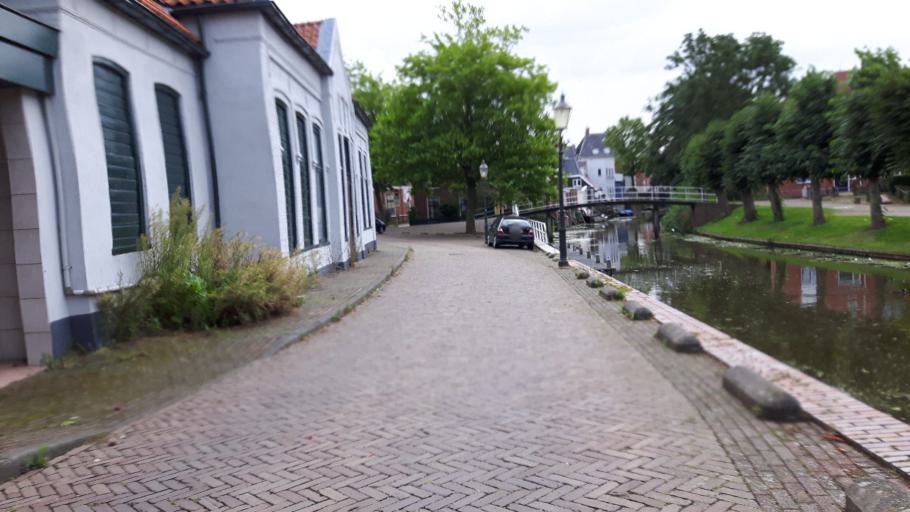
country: NL
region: Groningen
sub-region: Gemeente Appingedam
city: Appingedam
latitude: 53.3217
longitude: 6.8538
